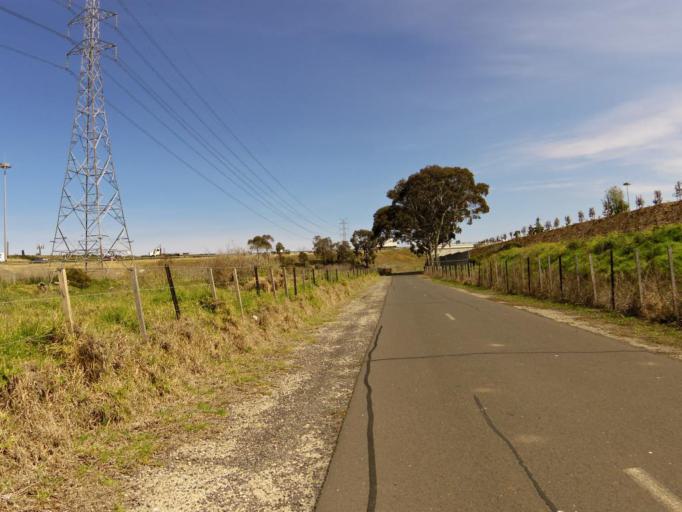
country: AU
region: Victoria
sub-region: Brimbank
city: Brooklyn
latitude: -37.8245
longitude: 144.8152
